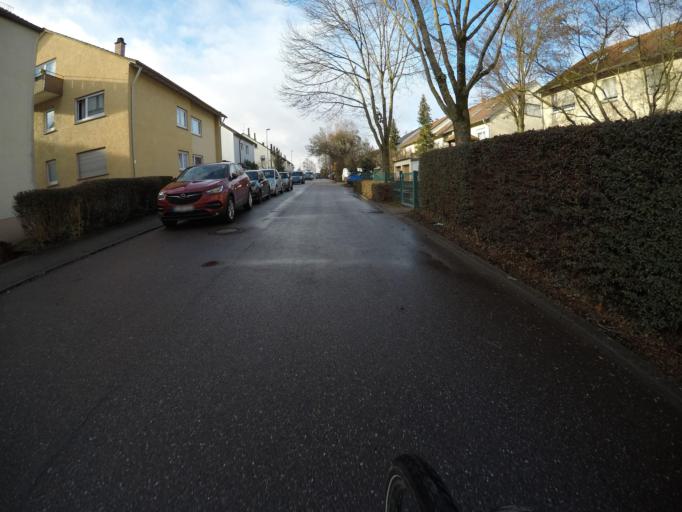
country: DE
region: Baden-Wuerttemberg
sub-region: Regierungsbezirk Stuttgart
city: Ditzingen
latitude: 48.8229
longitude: 9.0651
